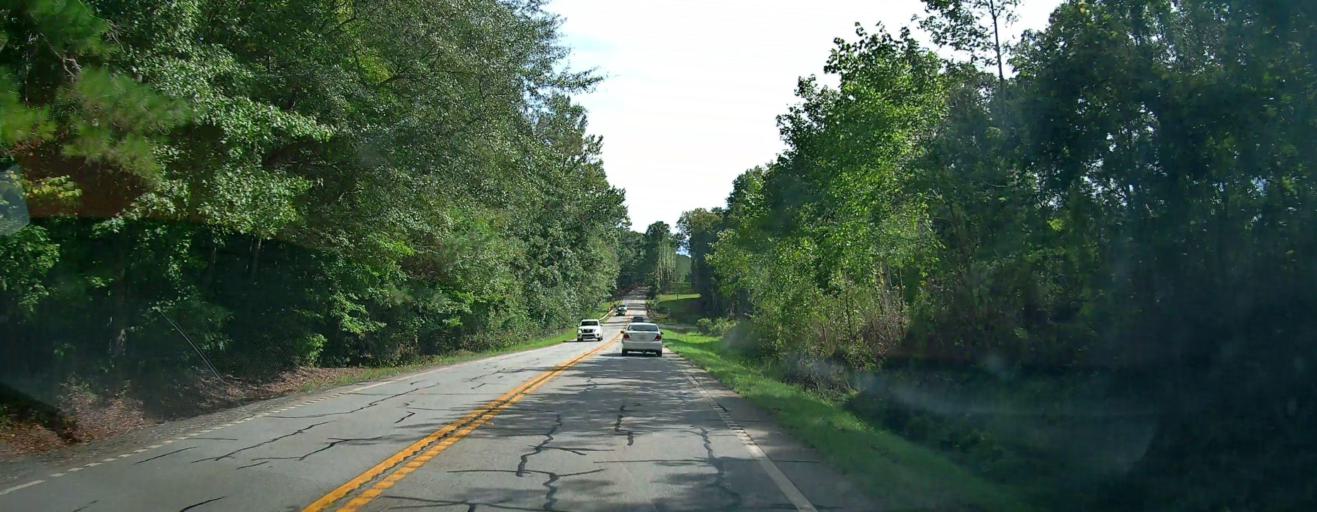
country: US
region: Georgia
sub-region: Harris County
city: Hamilton
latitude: 32.6908
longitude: -84.8568
